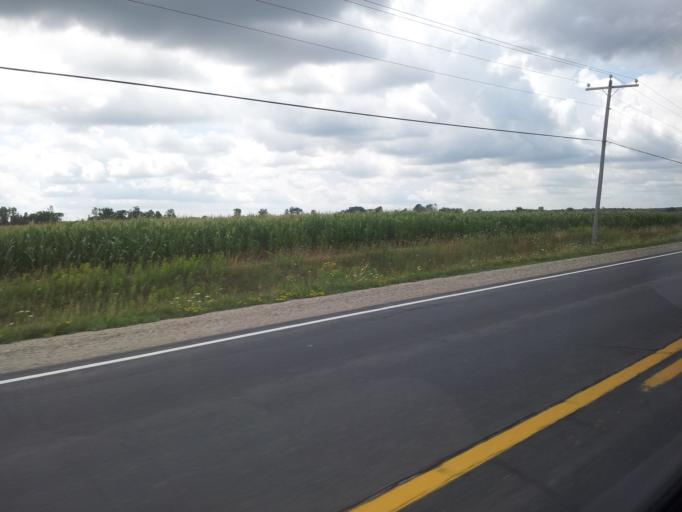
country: CA
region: Ontario
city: Stratford
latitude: 43.3699
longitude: -80.8682
